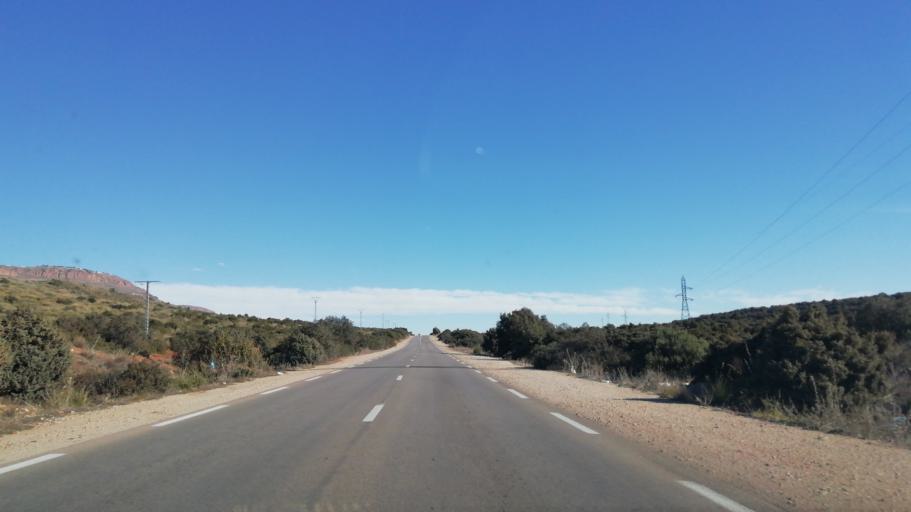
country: DZ
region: Tlemcen
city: Sebdou
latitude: 34.7168
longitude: -1.2041
